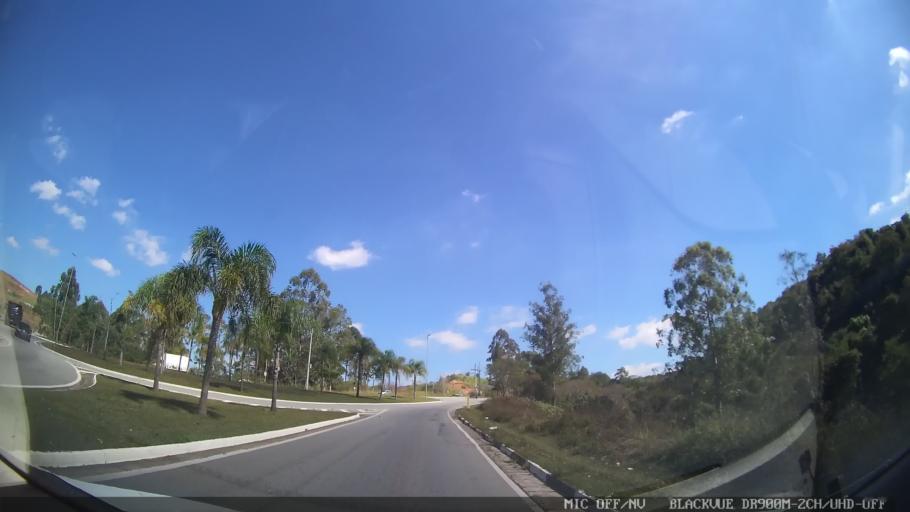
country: BR
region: Sao Paulo
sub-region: Carapicuiba
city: Carapicuiba
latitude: -23.4423
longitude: -46.8332
